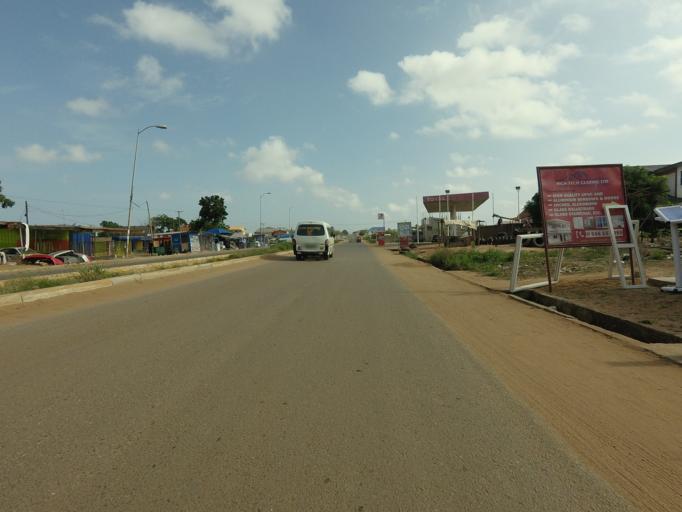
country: GH
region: Greater Accra
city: Tema
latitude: 5.6724
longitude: -0.0456
